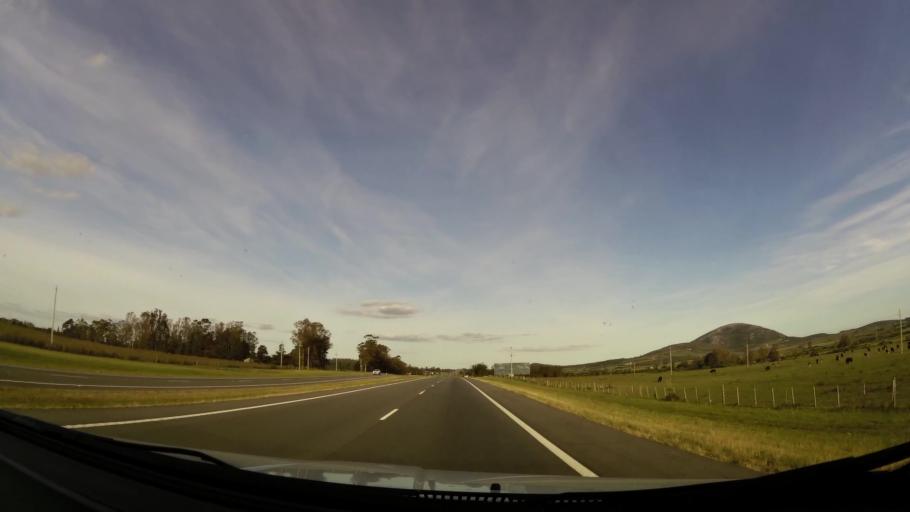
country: UY
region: Maldonado
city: Pan de Azucar
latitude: -34.7905
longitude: -55.3069
